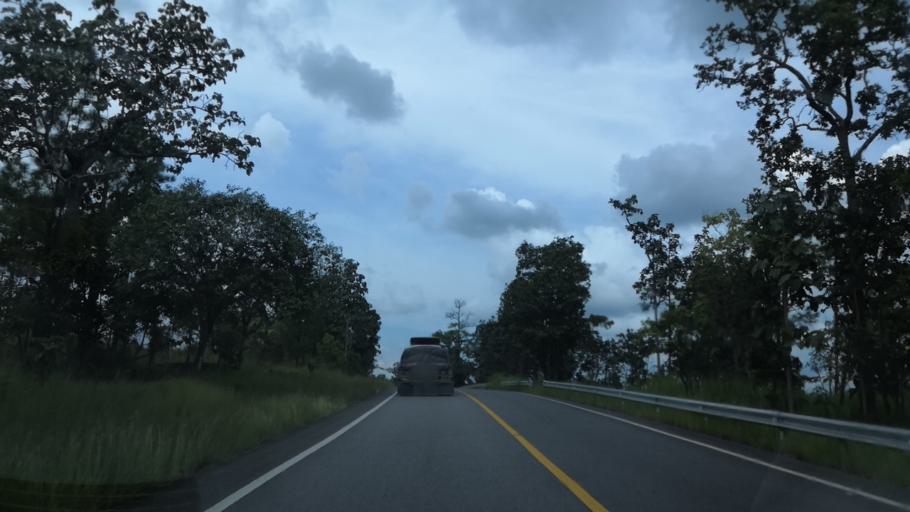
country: TH
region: Mae Hong Son
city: Khun Yuam
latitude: 18.7939
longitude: 97.9327
